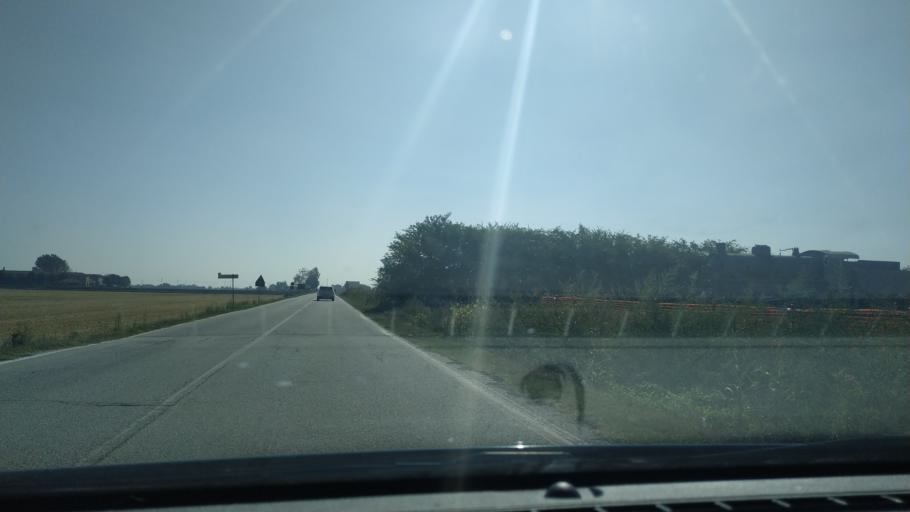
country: IT
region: Piedmont
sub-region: Provincia di Alessandria
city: Borgo San Martino
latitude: 45.1006
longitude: 8.5276
